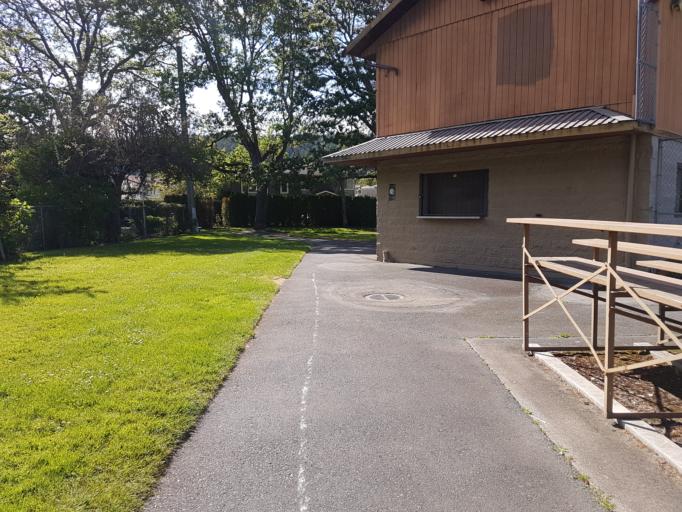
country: CA
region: British Columbia
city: Oak Bay
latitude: 48.4870
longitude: -123.3336
